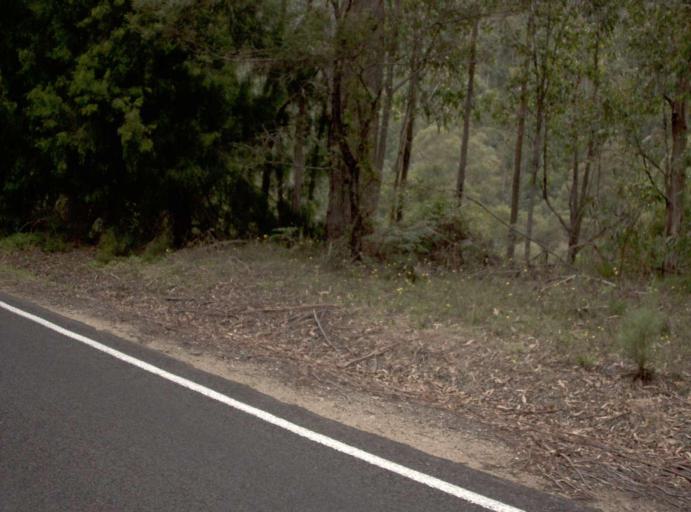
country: AU
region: New South Wales
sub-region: Bombala
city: Bombala
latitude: -37.4073
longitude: 149.1998
